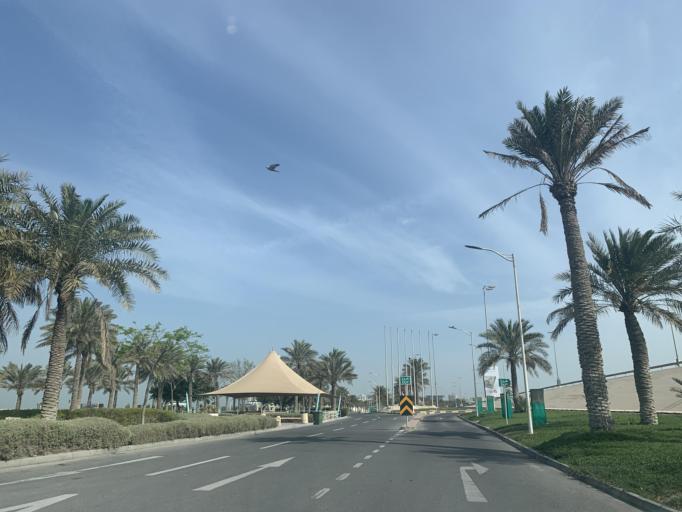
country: BH
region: Muharraq
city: Al Muharraq
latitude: 26.2511
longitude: 50.6044
